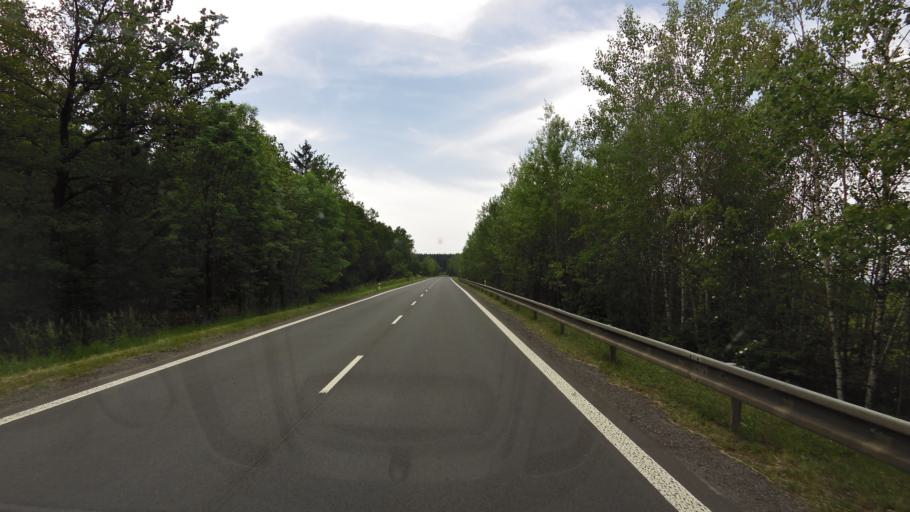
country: CZ
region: Plzensky
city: St'ahlavy
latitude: 49.7035
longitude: 13.5371
